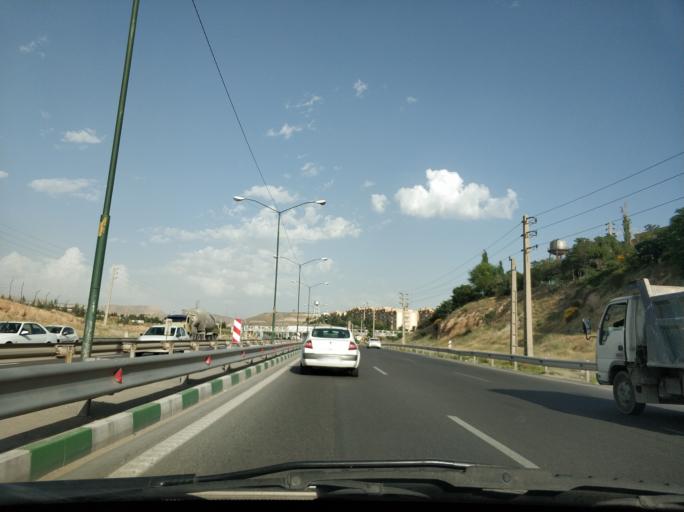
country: IR
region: Tehran
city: Tajrish
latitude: 35.7468
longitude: 51.5969
